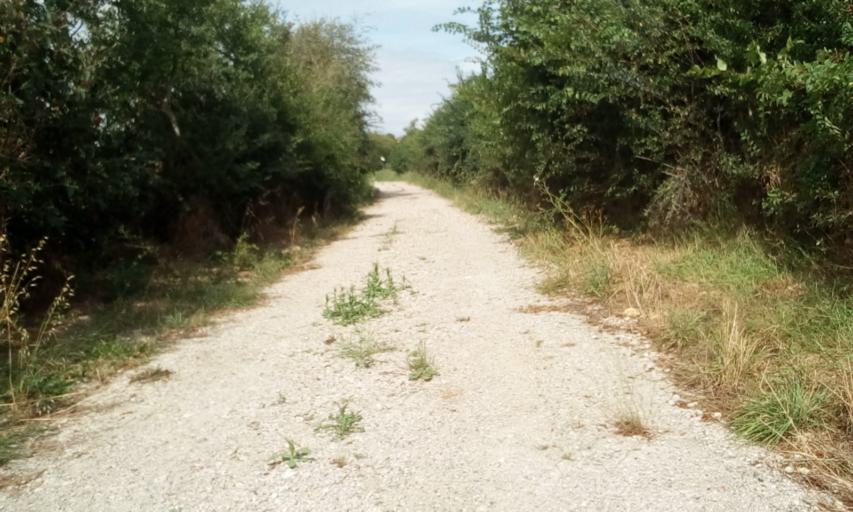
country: FR
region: Lower Normandy
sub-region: Departement du Calvados
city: Amfreville
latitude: 49.2358
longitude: -0.2309
